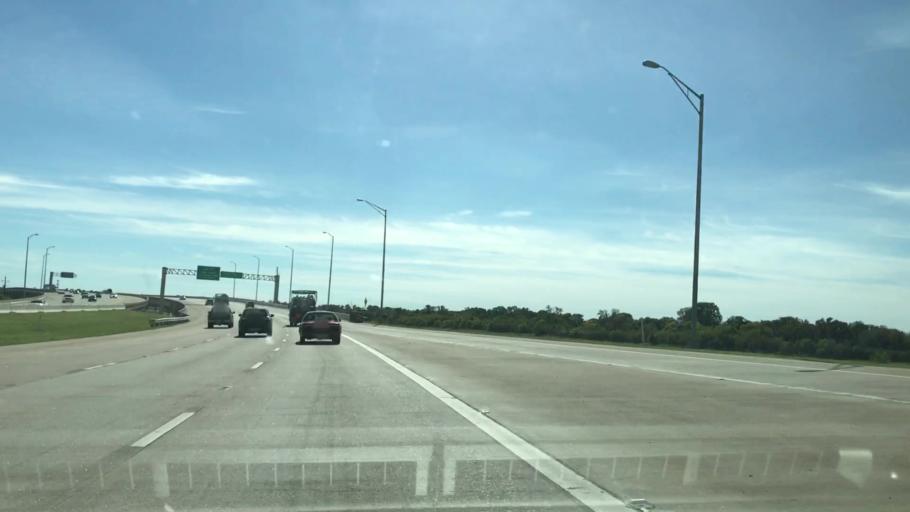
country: US
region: Texas
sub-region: Dallas County
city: Farmers Branch
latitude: 32.9443
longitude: -96.9293
